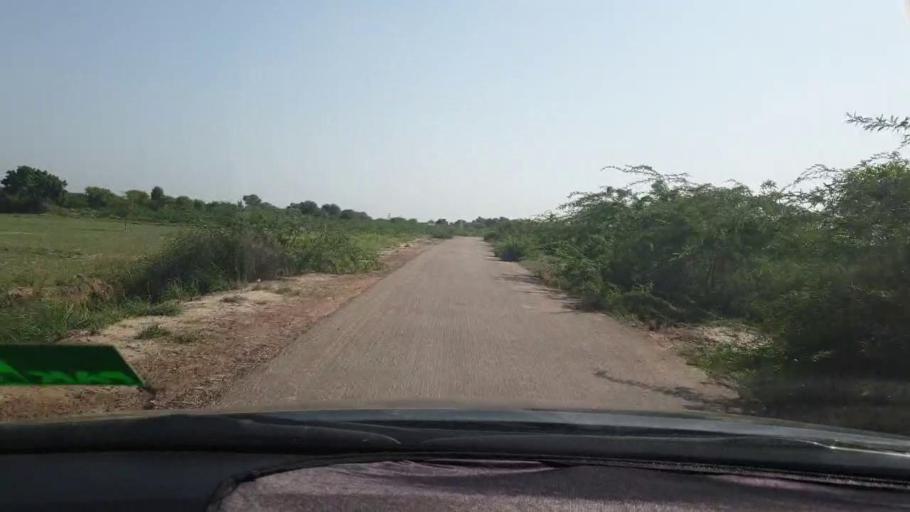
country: PK
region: Sindh
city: Naukot
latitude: 24.9483
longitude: 69.2486
